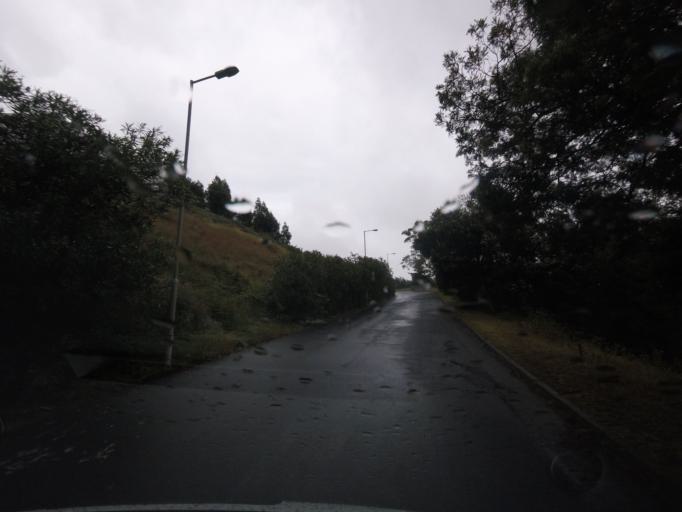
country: PT
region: Madeira
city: Canico
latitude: 32.6501
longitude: -16.8601
